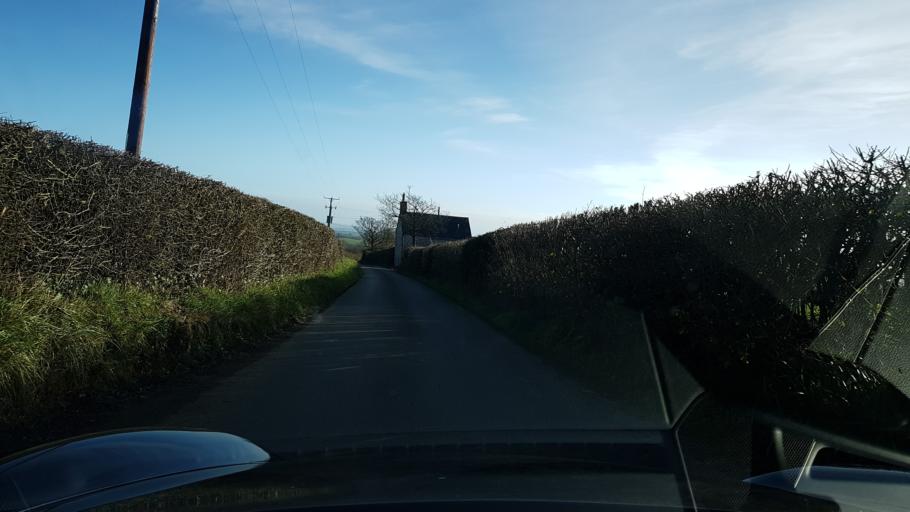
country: GB
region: England
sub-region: Dorset
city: Lyme Regis
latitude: 50.7860
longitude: -2.8613
